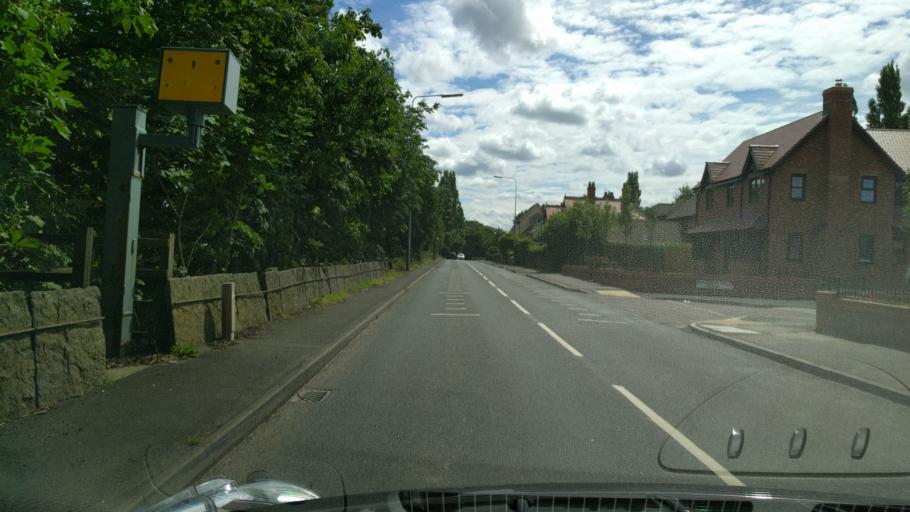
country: GB
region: England
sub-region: Warrington
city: Culcheth
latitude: 53.4632
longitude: -2.4929
